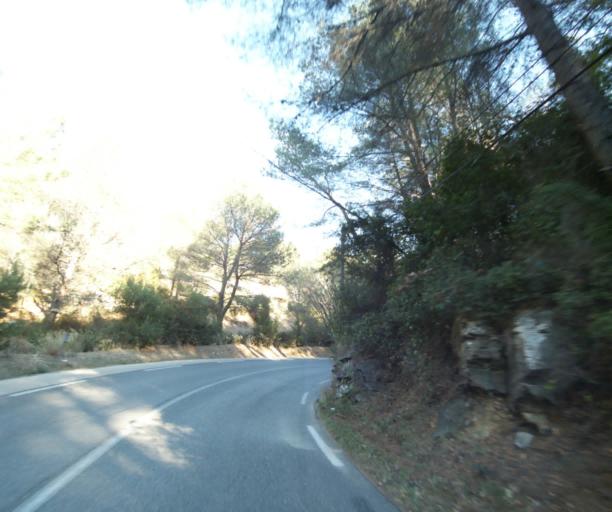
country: FR
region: Provence-Alpes-Cote d'Azur
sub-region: Departement des Bouches-du-Rhone
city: La Ciotat
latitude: 43.1970
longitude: 5.5942
